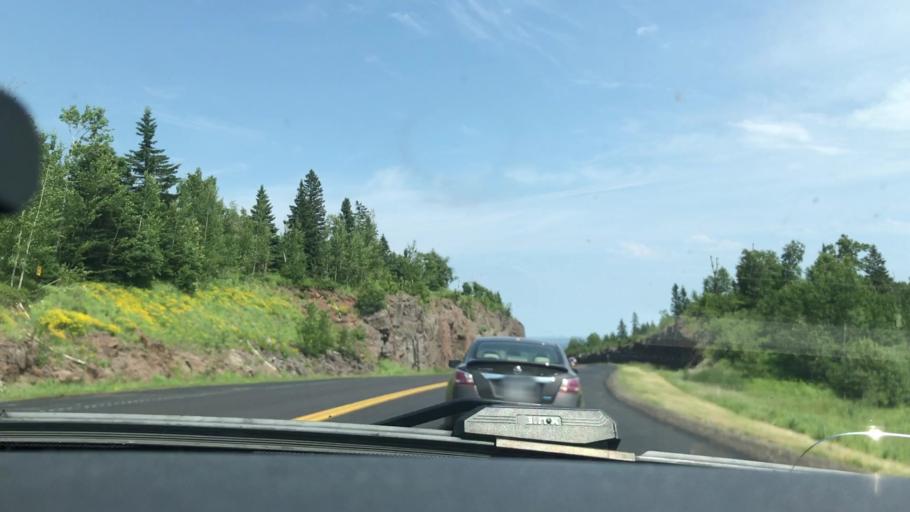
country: US
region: Minnesota
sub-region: Lake County
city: Two Harbors
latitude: 47.1465
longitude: -91.4595
